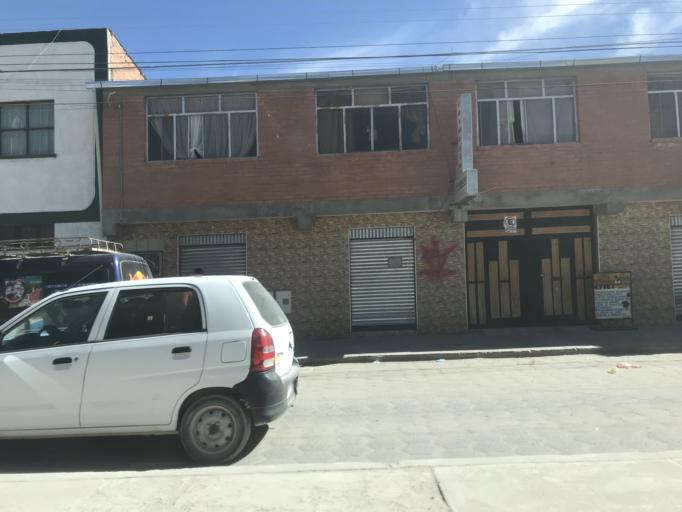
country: BO
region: Potosi
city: Uyuni
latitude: -20.4632
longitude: -66.8260
